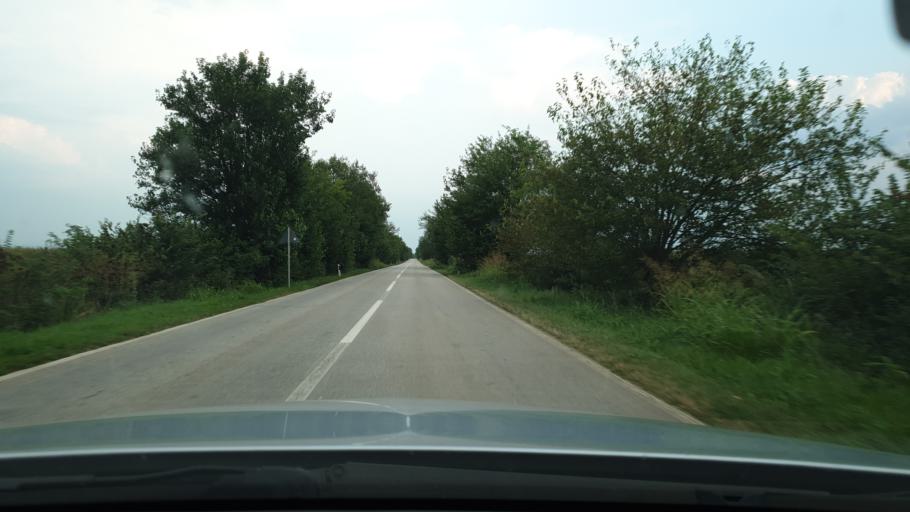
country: RS
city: Izbiste
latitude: 45.0006
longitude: 21.2809
